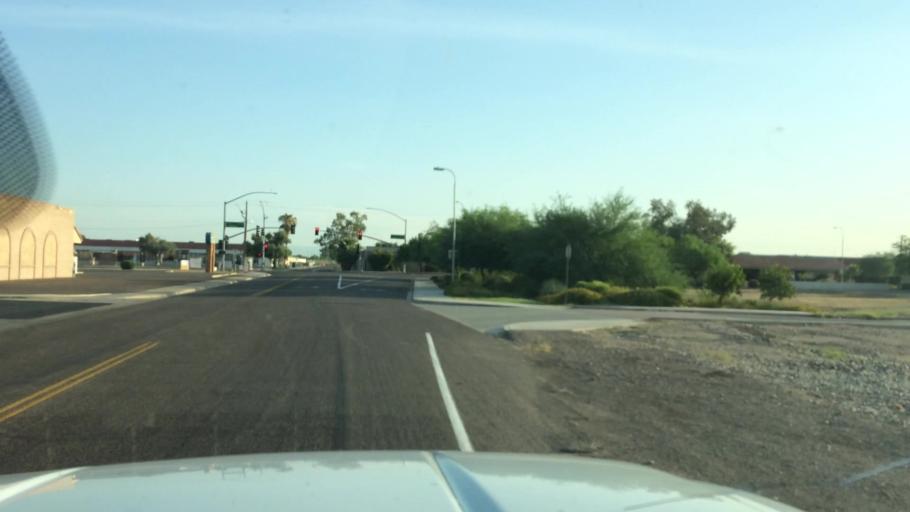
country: US
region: Arizona
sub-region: Maricopa County
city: Sun City
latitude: 33.5794
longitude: -112.2634
